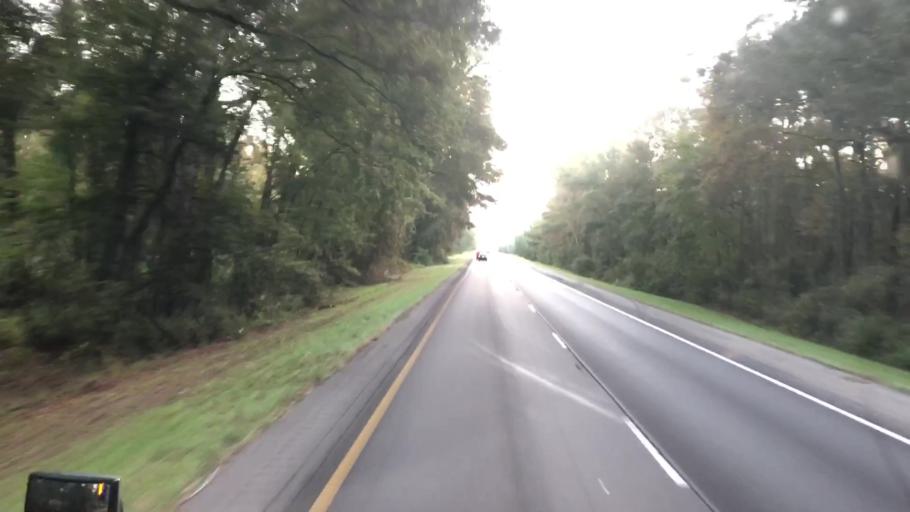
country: US
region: South Carolina
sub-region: Clarendon County
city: Manning
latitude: 33.5705
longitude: -80.3839
